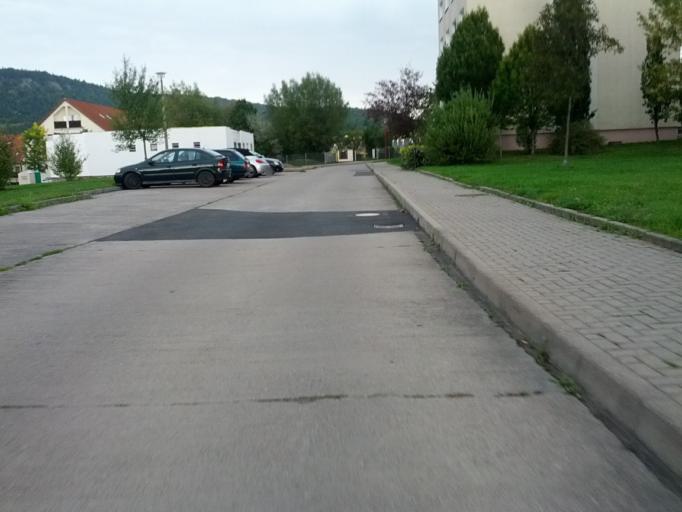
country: DE
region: Thuringia
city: Thal
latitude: 50.9525
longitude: 10.3971
